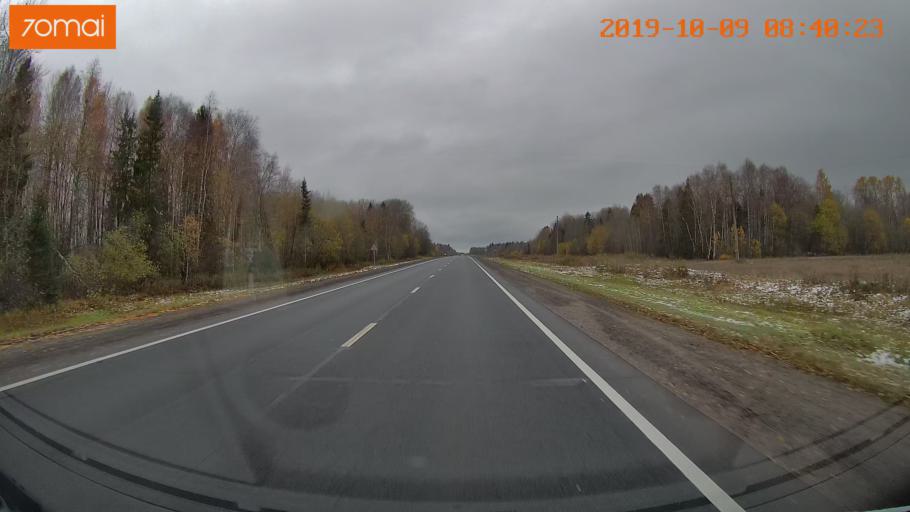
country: RU
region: Vologda
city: Gryazovets
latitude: 58.9858
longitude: 40.1410
